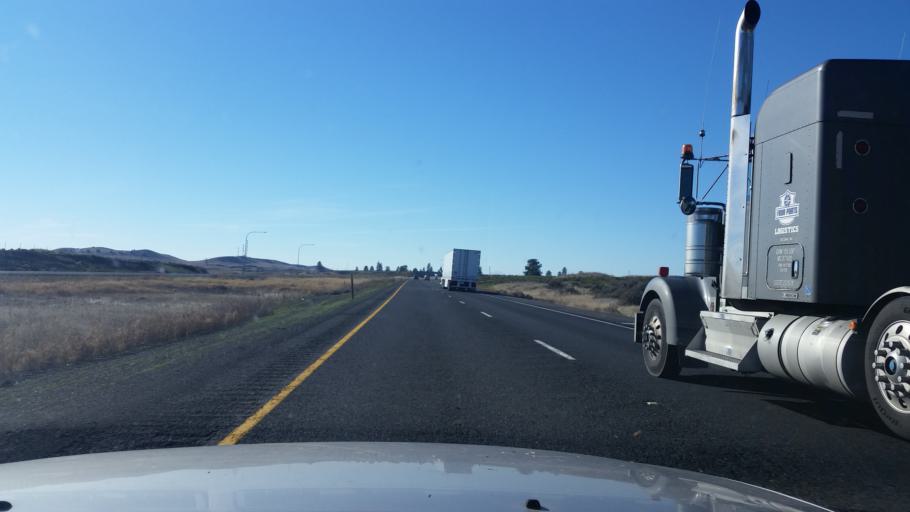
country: US
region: Washington
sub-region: Spokane County
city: Medical Lake
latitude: 47.4016
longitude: -117.8339
